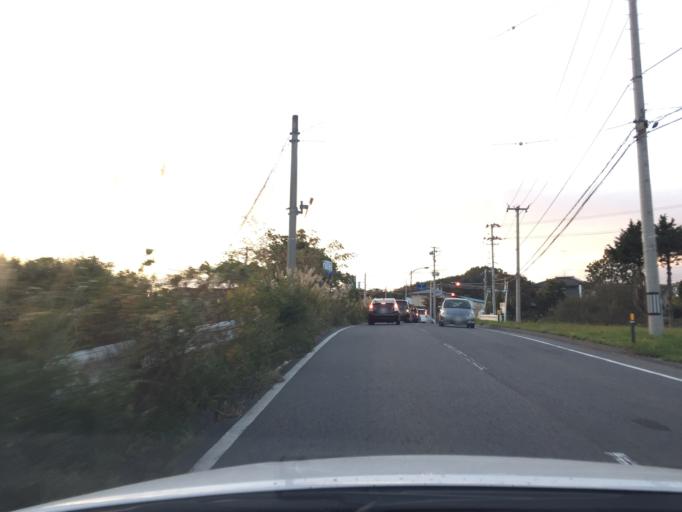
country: JP
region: Fukushima
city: Miharu
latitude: 37.3896
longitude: 140.4440
